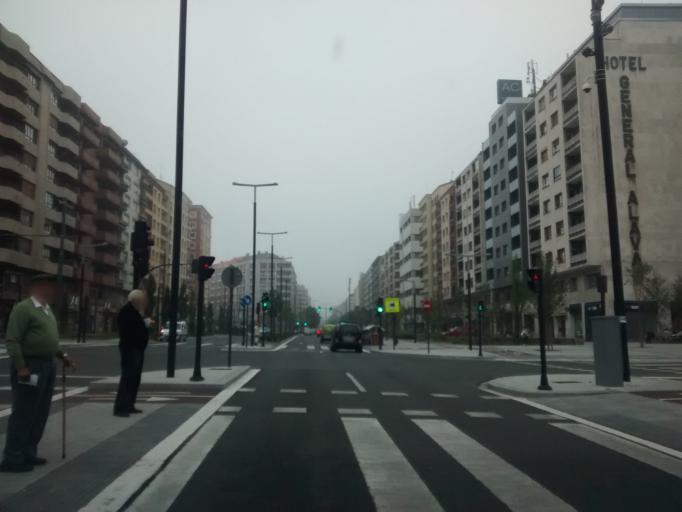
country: ES
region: Basque Country
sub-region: Provincia de Alava
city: Gasteiz / Vitoria
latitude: 42.8515
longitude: -2.6807
